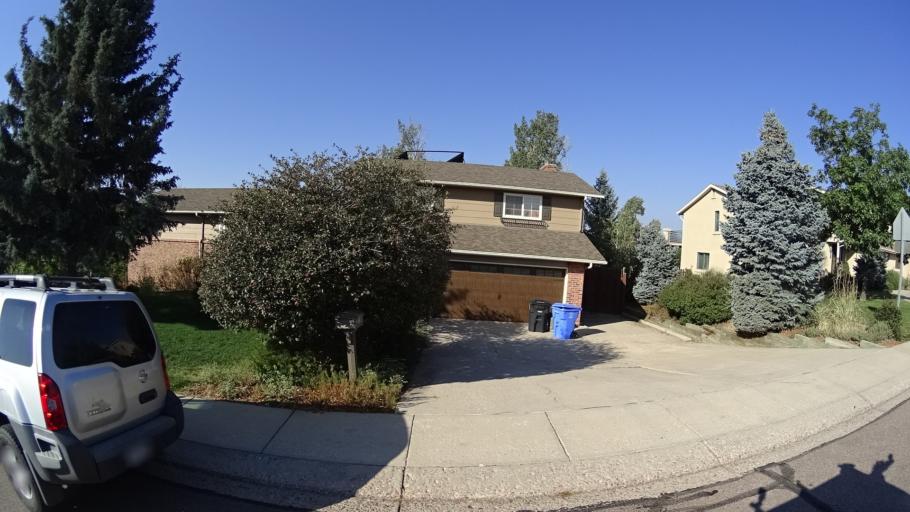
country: US
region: Colorado
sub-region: El Paso County
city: Cimarron Hills
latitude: 38.8923
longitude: -104.7278
